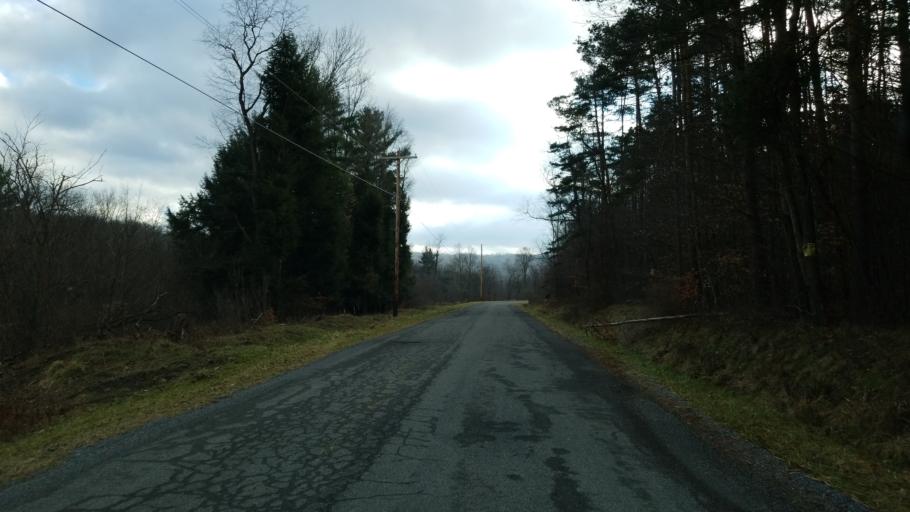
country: US
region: Pennsylvania
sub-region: Clearfield County
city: Treasure Lake
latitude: 41.1339
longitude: -78.6031
